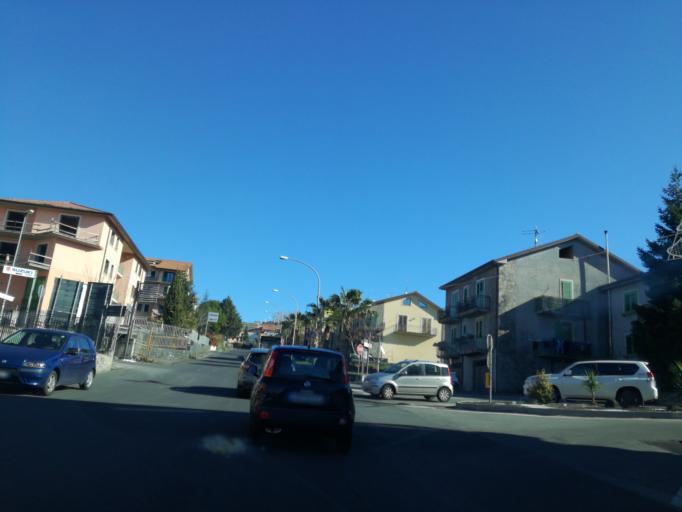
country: IT
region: Sicily
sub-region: Catania
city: Bronte
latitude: 37.7914
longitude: 14.8426
